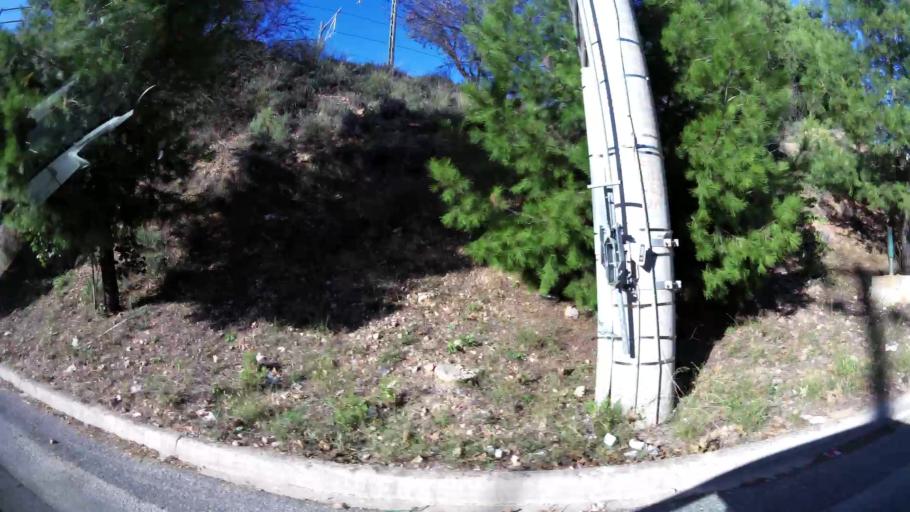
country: GR
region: Attica
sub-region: Nomarchia Anatolikis Attikis
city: Kryoneri
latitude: 38.1260
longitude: 23.8371
